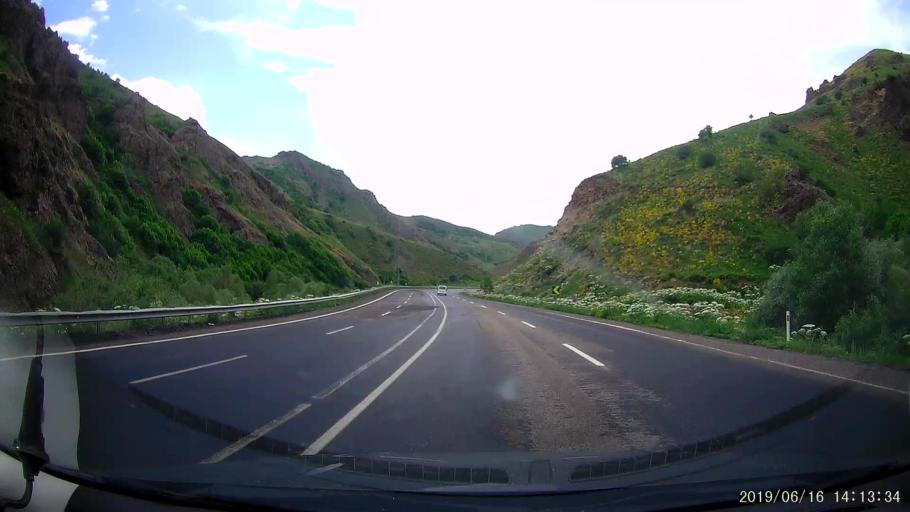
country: TR
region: Agri
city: Tahir
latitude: 39.7966
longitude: 42.5142
